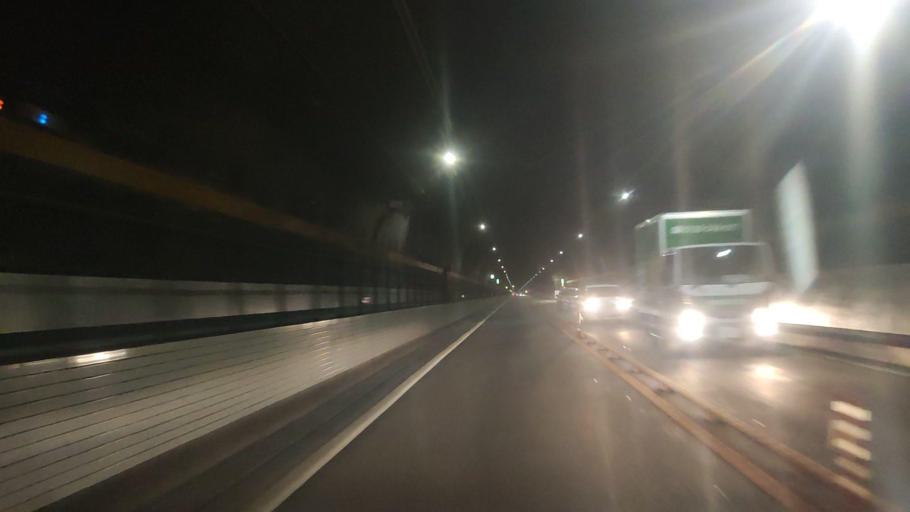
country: JP
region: Nagasaki
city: Obita
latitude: 32.7853
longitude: 129.8834
